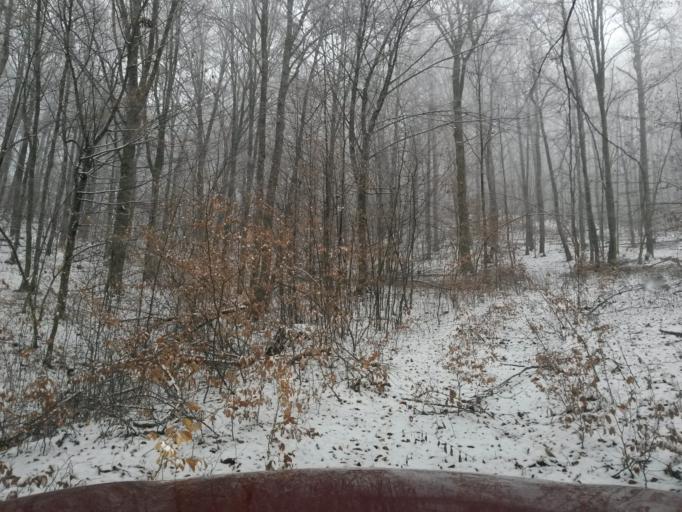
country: SK
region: Presovsky
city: Sabinov
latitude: 48.9767
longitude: 21.0899
